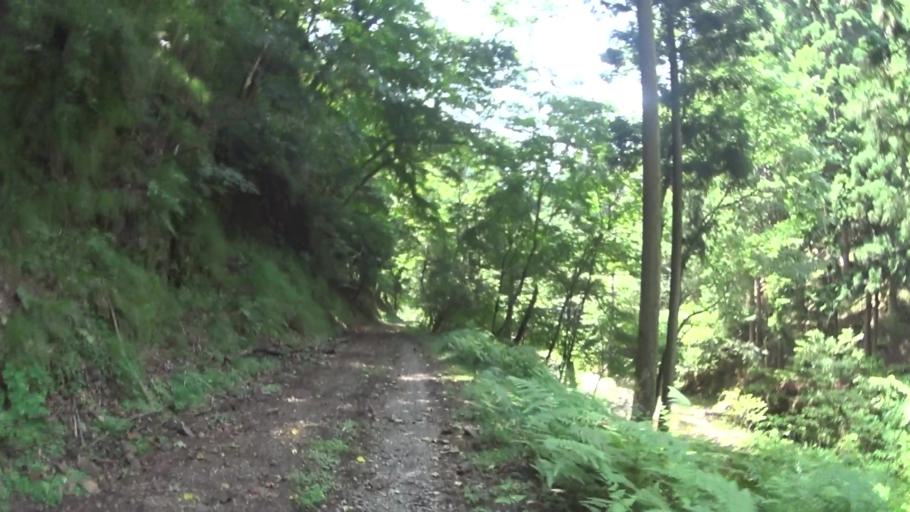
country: JP
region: Kyoto
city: Maizuru
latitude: 35.3267
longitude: 135.4610
